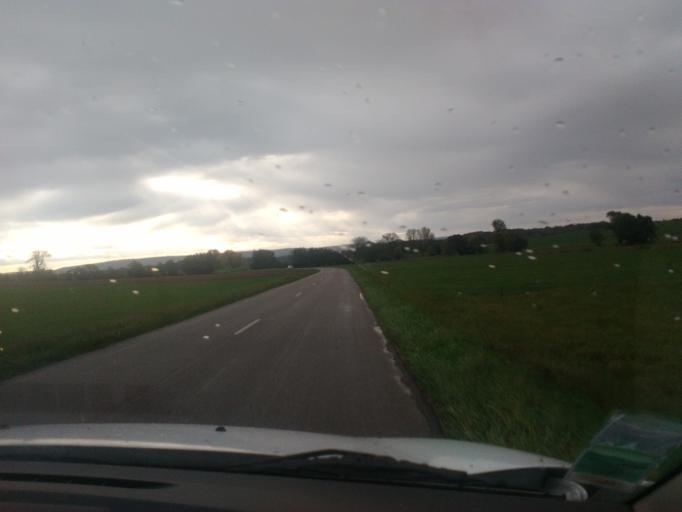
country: FR
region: Lorraine
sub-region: Departement des Vosges
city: Aydoilles
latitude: 48.2567
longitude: 6.5442
